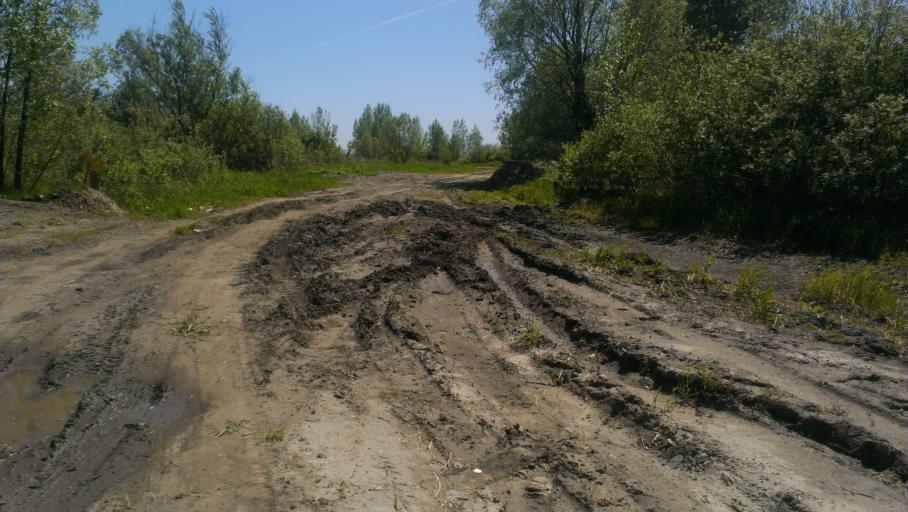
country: RU
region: Altai Krai
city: Zaton
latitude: 53.3138
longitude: 83.8518
